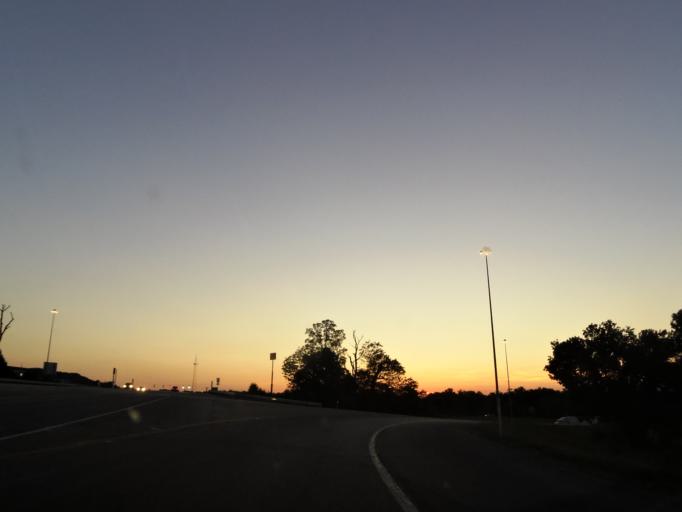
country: US
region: Kentucky
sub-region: Madison County
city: Berea
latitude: 37.5688
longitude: -84.3129
